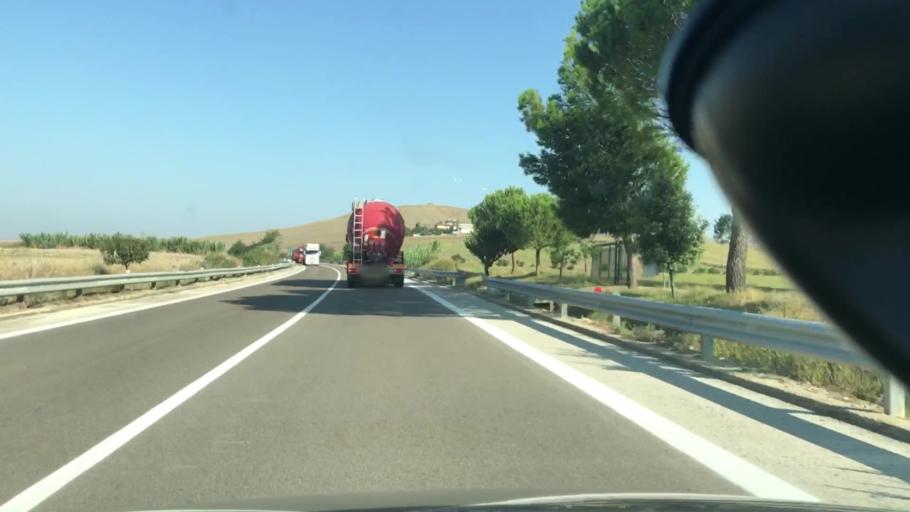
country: IT
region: Basilicate
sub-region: Provincia di Matera
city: Irsina
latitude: 40.8067
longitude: 16.2727
